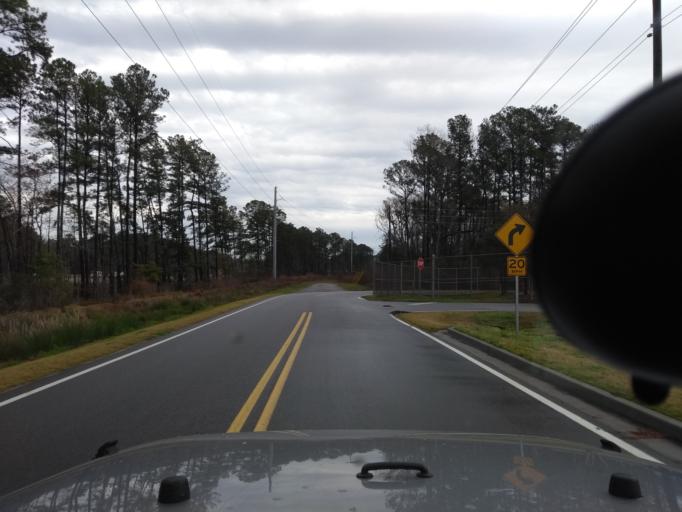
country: US
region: Georgia
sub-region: Chatham County
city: Garden City
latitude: 32.0685
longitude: -81.1665
